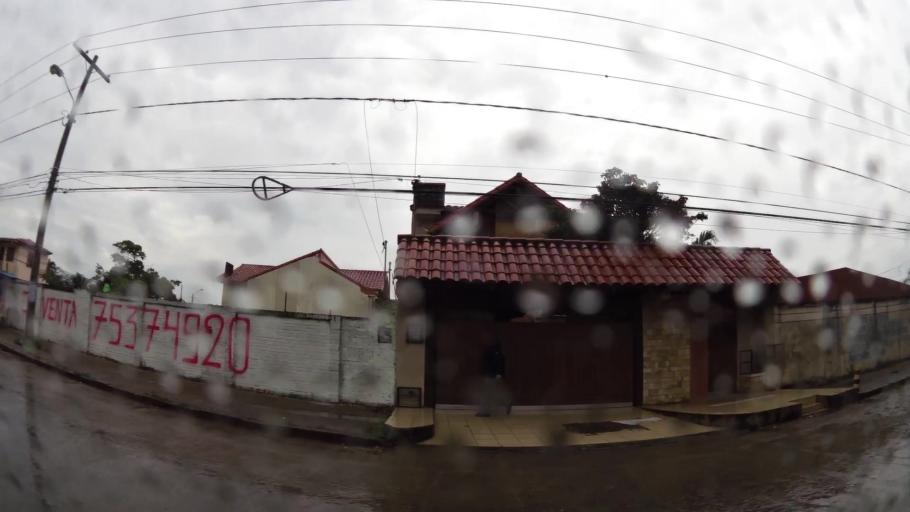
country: BO
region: Santa Cruz
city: Santa Cruz de la Sierra
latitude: -17.7756
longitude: -63.1490
